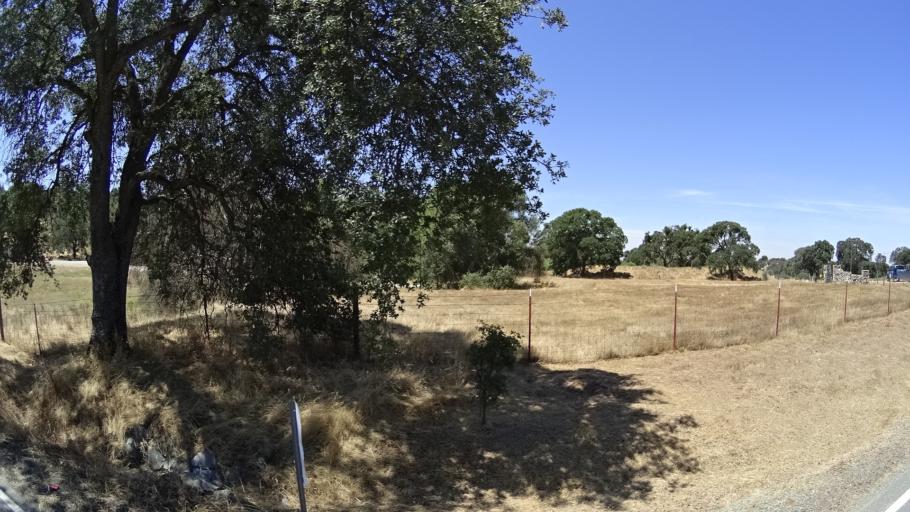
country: US
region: California
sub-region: Calaveras County
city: Rancho Calaveras
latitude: 38.1412
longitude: -120.8957
